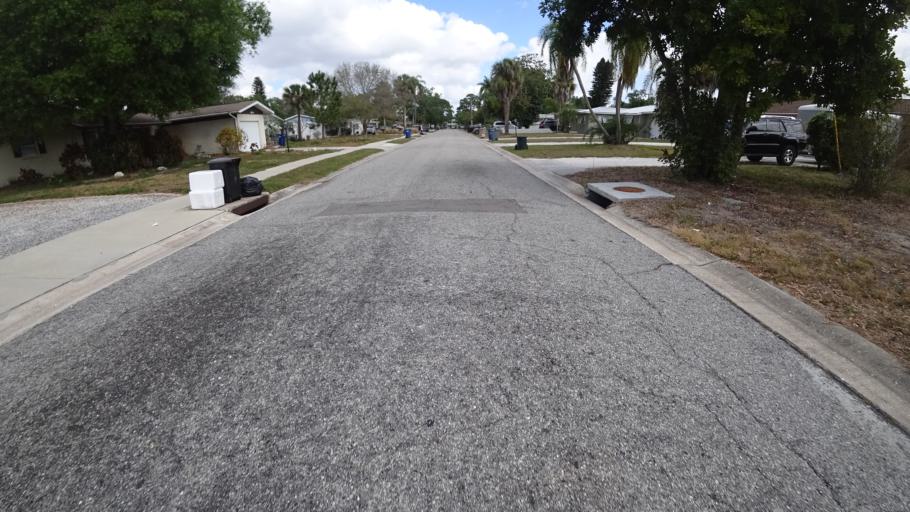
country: US
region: Florida
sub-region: Manatee County
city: Bayshore Gardens
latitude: 27.4327
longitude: -82.5810
